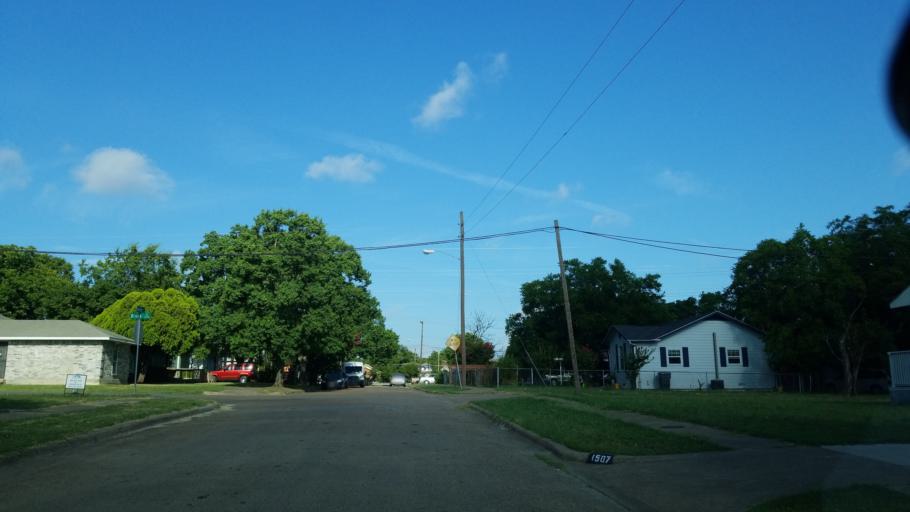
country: US
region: Texas
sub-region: Dallas County
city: Dallas
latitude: 32.7267
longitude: -96.8031
